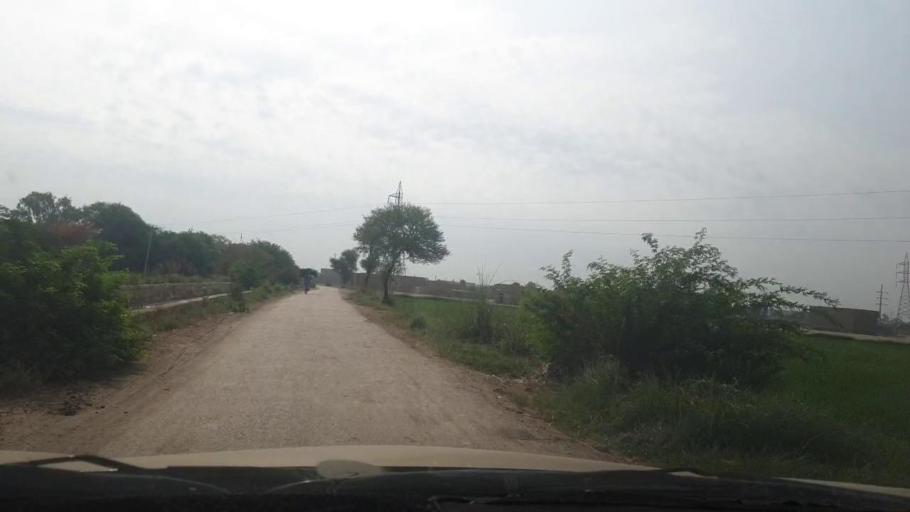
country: PK
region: Sindh
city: Larkana
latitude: 27.5821
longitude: 68.2010
